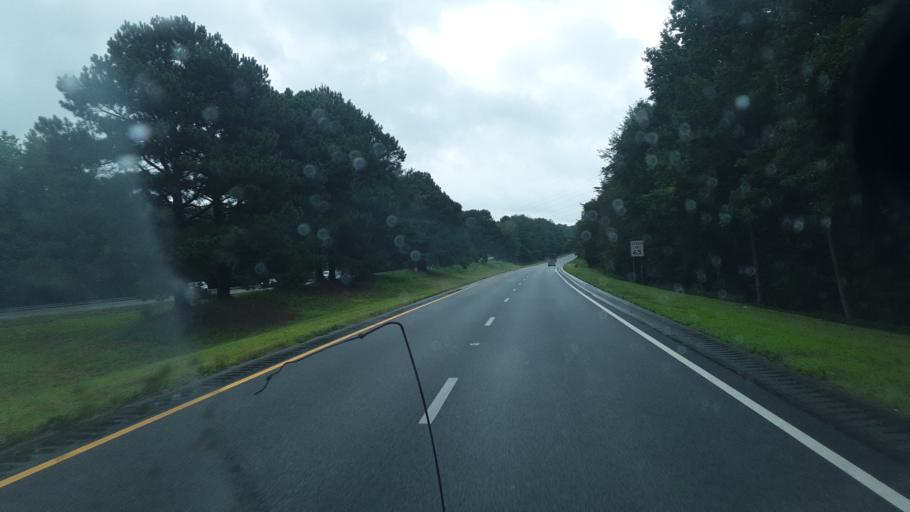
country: US
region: North Carolina
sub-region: Davidson County
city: Wallburg
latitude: 36.0368
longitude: -80.0904
